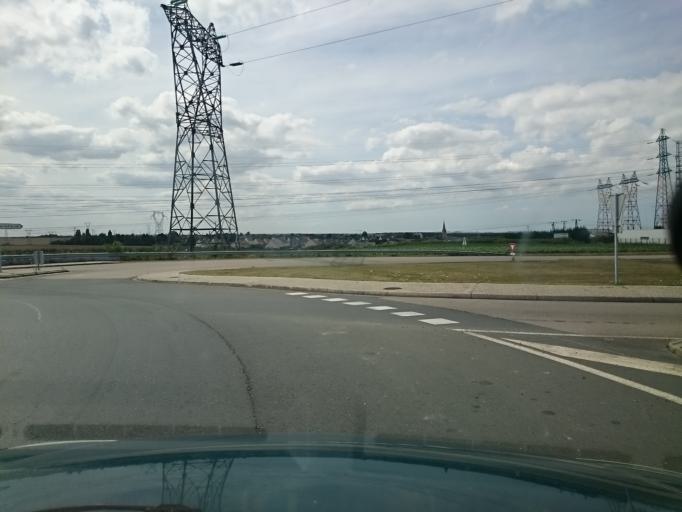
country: FR
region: Lower Normandy
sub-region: Departement du Calvados
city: Ifs
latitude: 49.1364
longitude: -0.3368
